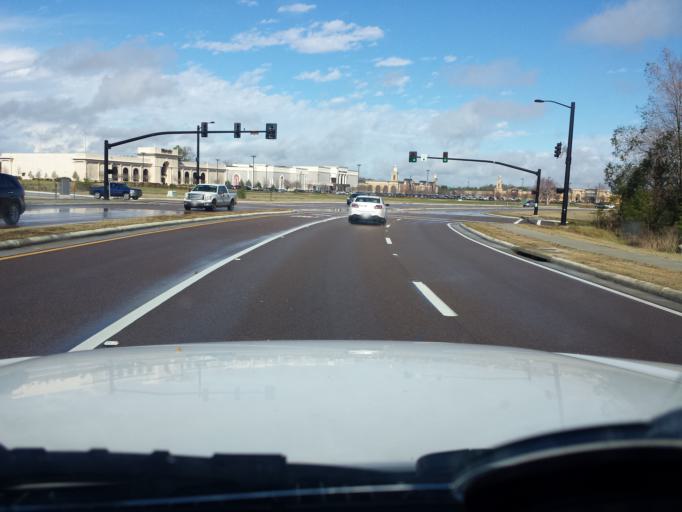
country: US
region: Mississippi
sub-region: Madison County
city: Madison
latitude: 32.4595
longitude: -90.1385
